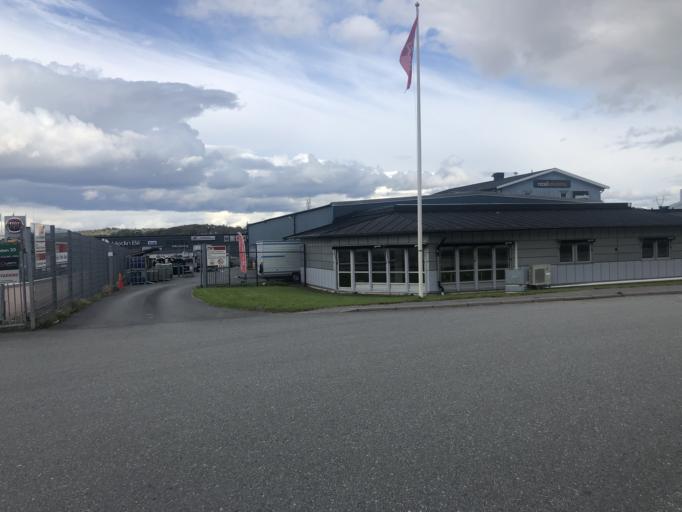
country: SE
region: Vaestra Goetaland
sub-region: Molndal
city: Moelndal
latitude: 57.6417
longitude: 12.0086
